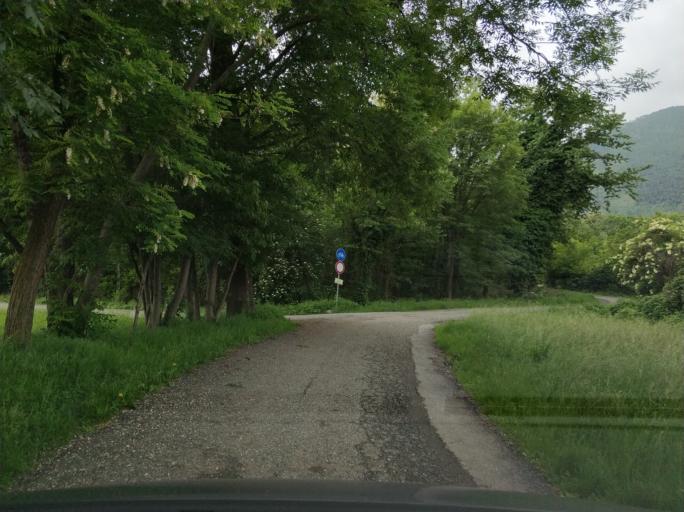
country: IT
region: Piedmont
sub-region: Provincia di Torino
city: Balangero
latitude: 45.2654
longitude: 7.5115
